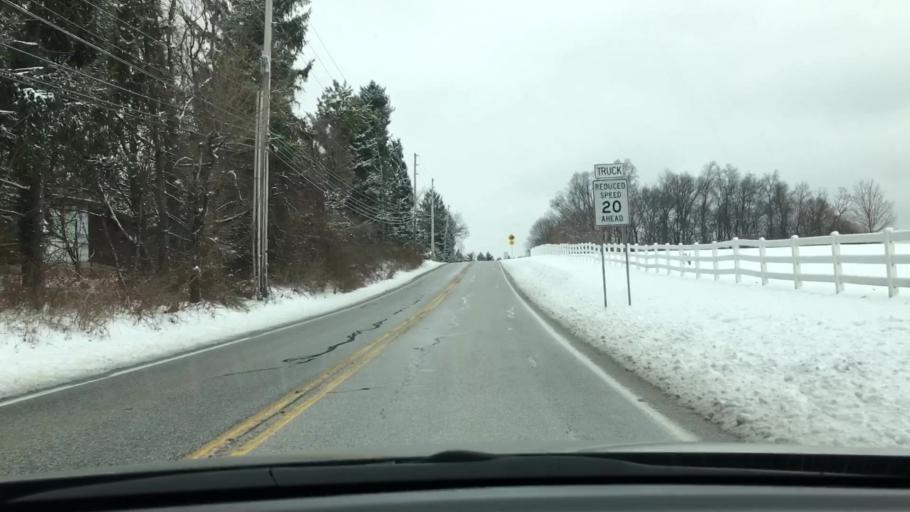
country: US
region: Pennsylvania
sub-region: York County
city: Grantley
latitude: 39.9302
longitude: -76.7255
